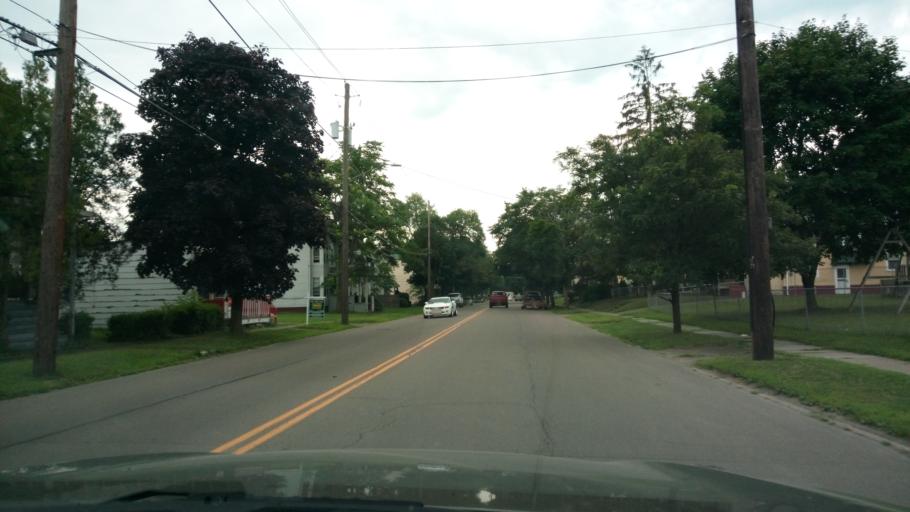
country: US
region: New York
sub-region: Chemung County
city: Elmira
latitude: 42.1071
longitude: -76.8056
